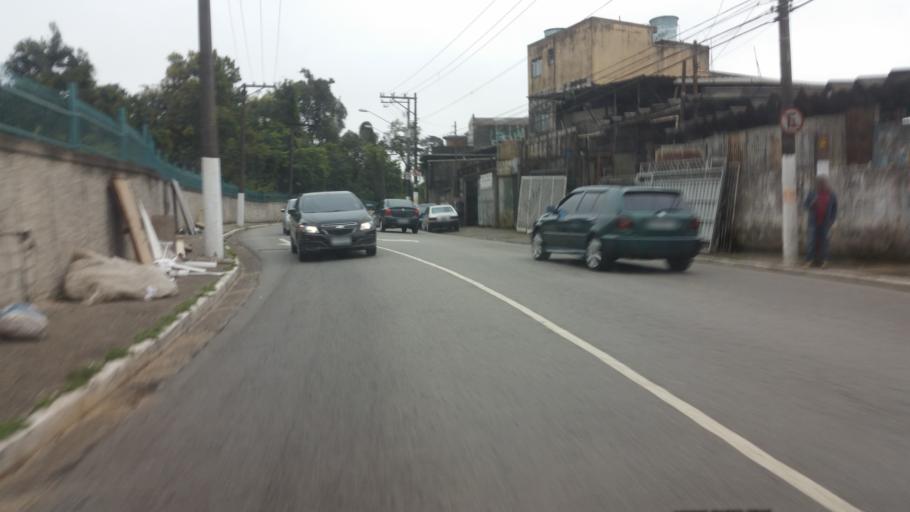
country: BR
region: Sao Paulo
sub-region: Diadema
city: Diadema
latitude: -23.6418
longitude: -46.6133
